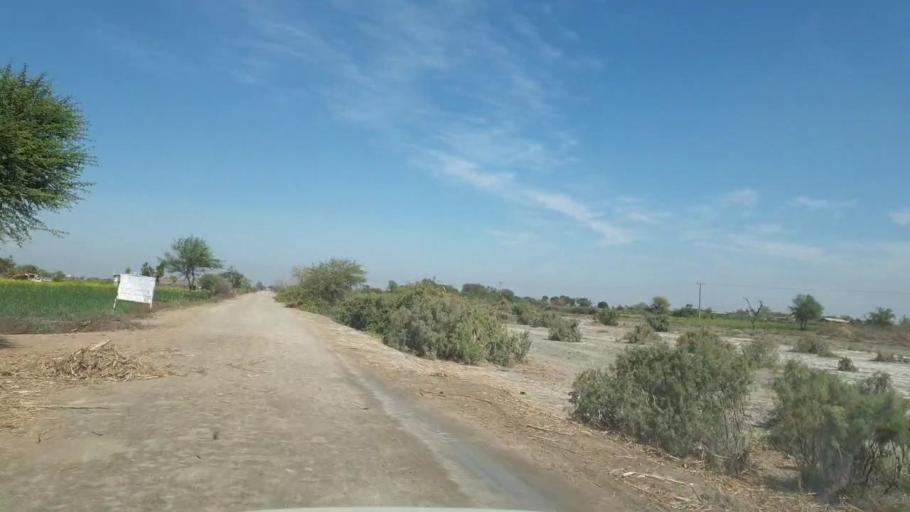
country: PK
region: Sindh
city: Pithoro
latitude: 25.6307
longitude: 69.2178
